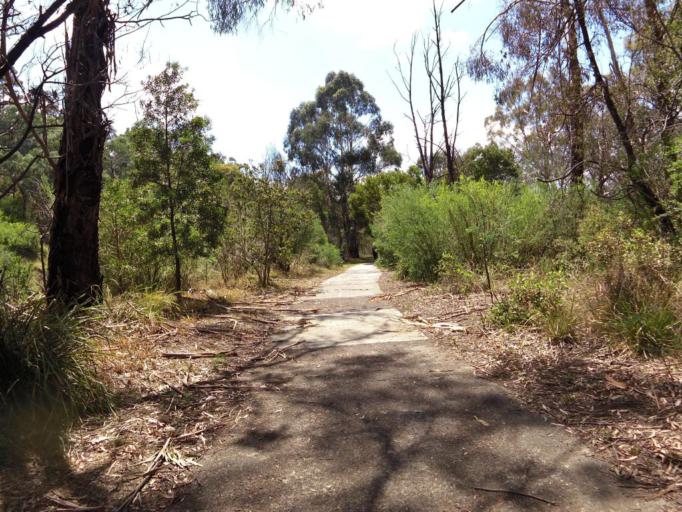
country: AU
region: Victoria
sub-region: Nillumbik
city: Diamond Creek
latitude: -37.6715
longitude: 145.1536
